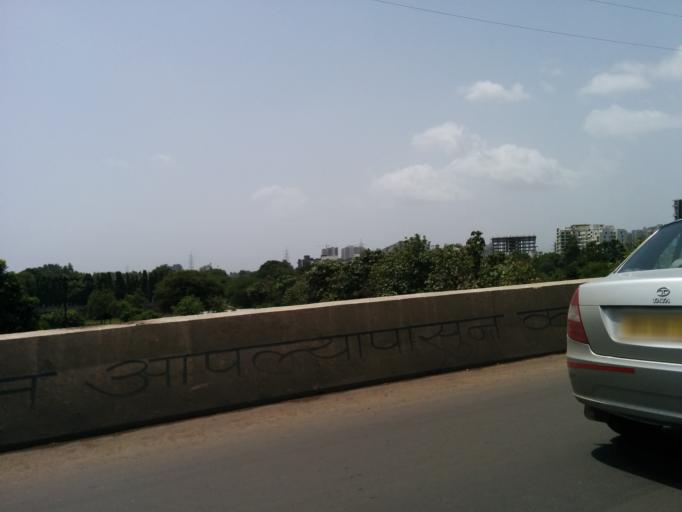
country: IN
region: Maharashtra
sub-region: Pune Division
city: Lohogaon
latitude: 18.5268
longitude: 73.9322
